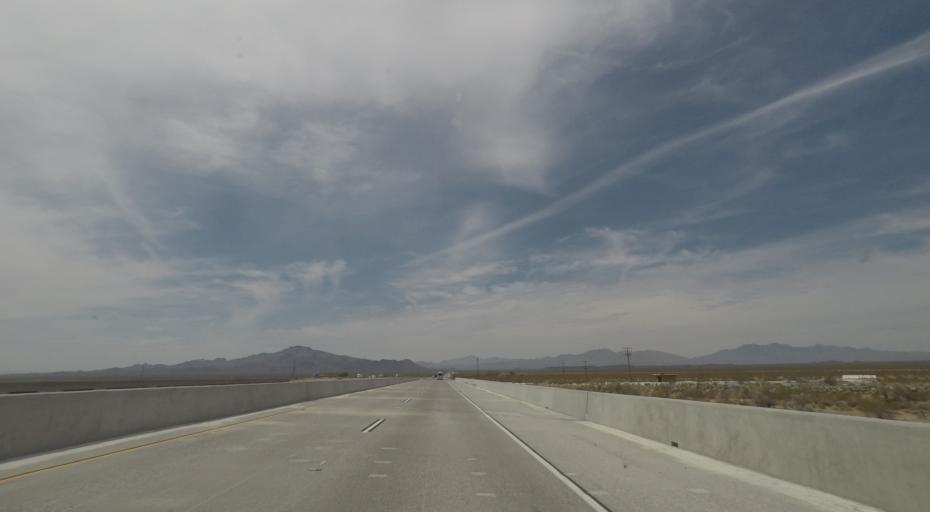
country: US
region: California
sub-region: San Bernardino County
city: Needles
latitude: 34.8104
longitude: -115.2109
